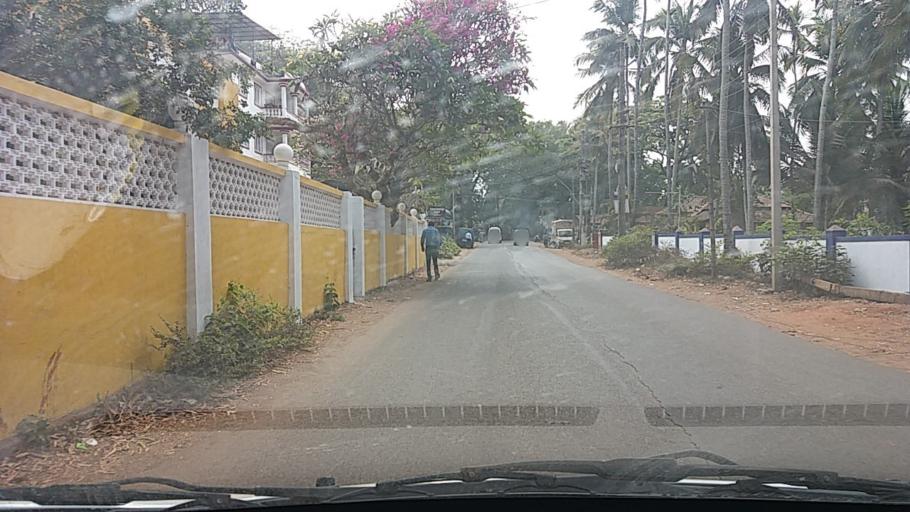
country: IN
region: Goa
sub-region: North Goa
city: Panaji
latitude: 15.5079
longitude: 73.8240
